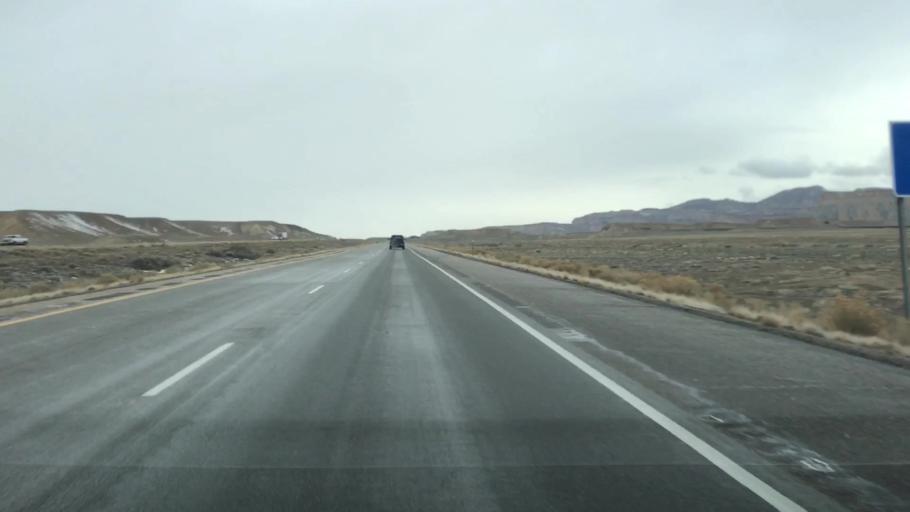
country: US
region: Utah
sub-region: Grand County
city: Moab
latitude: 38.9475
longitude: -109.6613
